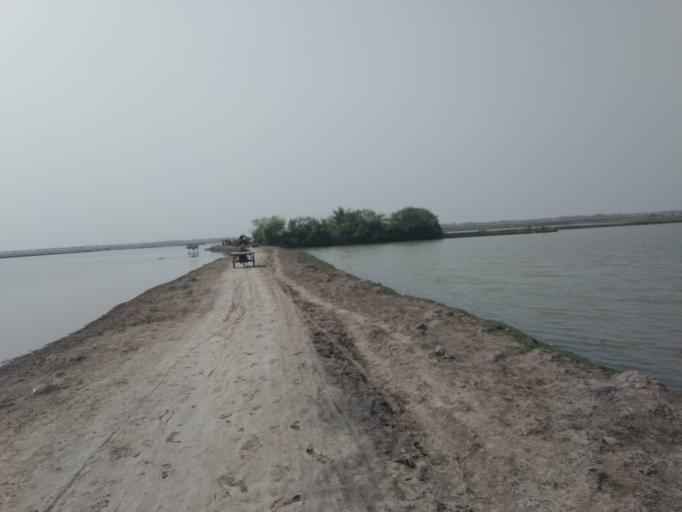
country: IN
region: West Bengal
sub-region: North 24 Parganas
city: Taki
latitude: 22.3439
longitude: 89.2325
